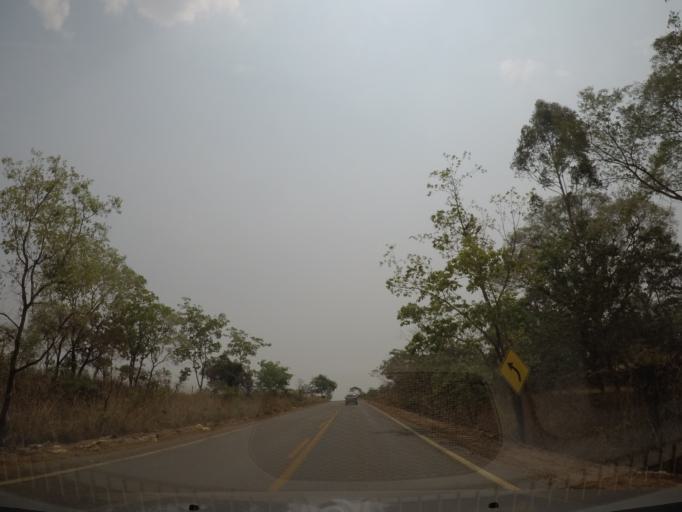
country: BR
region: Goias
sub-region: Pirenopolis
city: Pirenopolis
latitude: -15.8952
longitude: -48.8810
